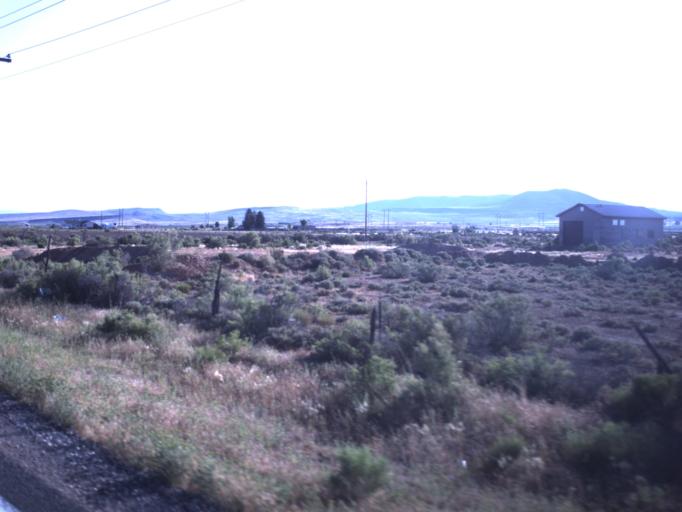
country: US
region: Utah
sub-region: Iron County
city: Enoch
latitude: 37.7940
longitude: -113.0506
